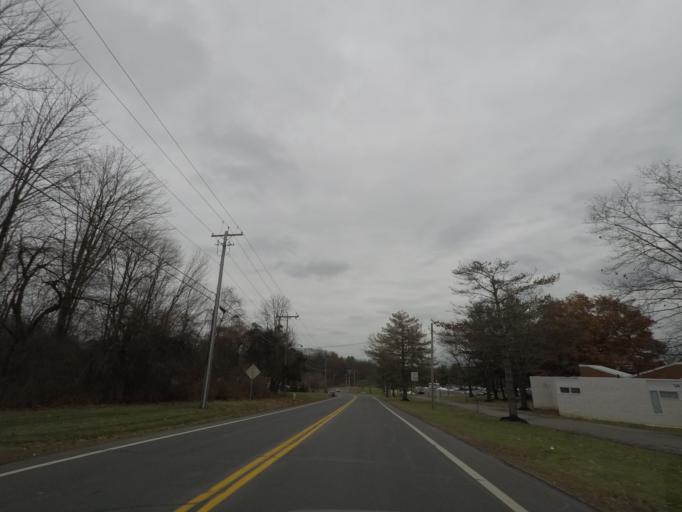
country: US
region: New York
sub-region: Schenectady County
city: Niskayuna
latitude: 42.7811
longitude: -73.8897
